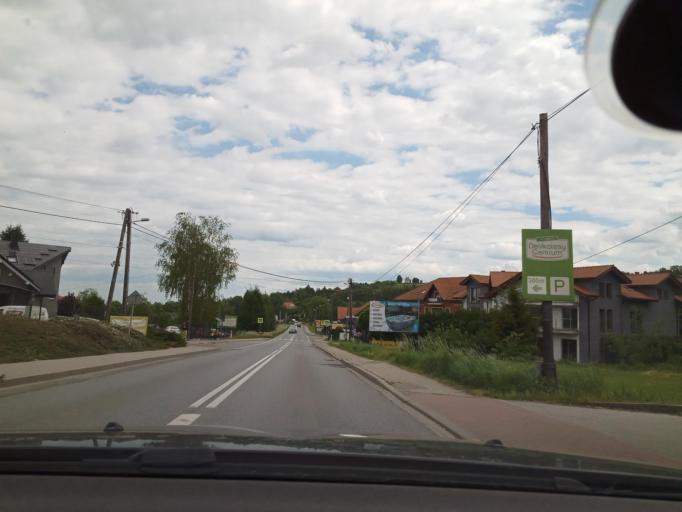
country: PL
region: Lesser Poland Voivodeship
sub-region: Powiat wielicki
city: Trabki
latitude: 49.9566
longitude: 20.1488
